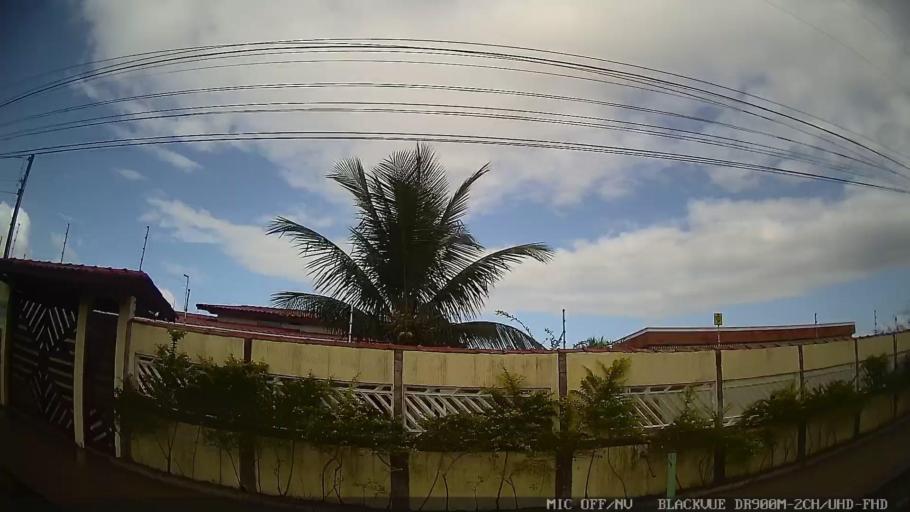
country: BR
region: Sao Paulo
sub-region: Itanhaem
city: Itanhaem
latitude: -24.2049
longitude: -46.8405
